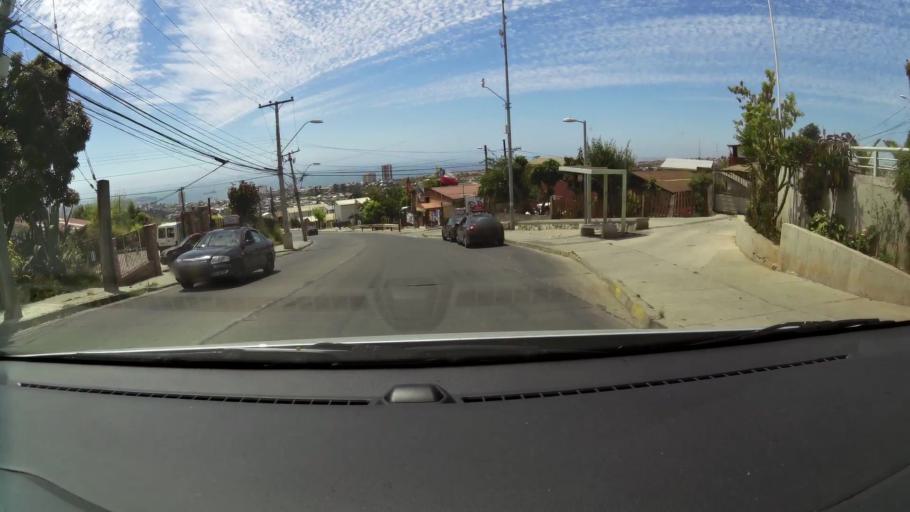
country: CL
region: Valparaiso
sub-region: Provincia de Valparaiso
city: Vina del Mar
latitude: -33.0610
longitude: -71.5740
